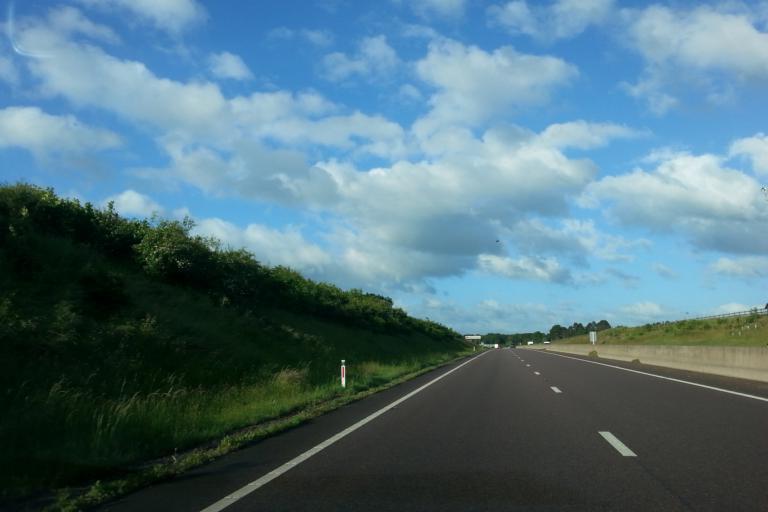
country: GB
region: England
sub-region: Nottinghamshire
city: Farndon
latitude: 53.0200
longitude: -0.8970
